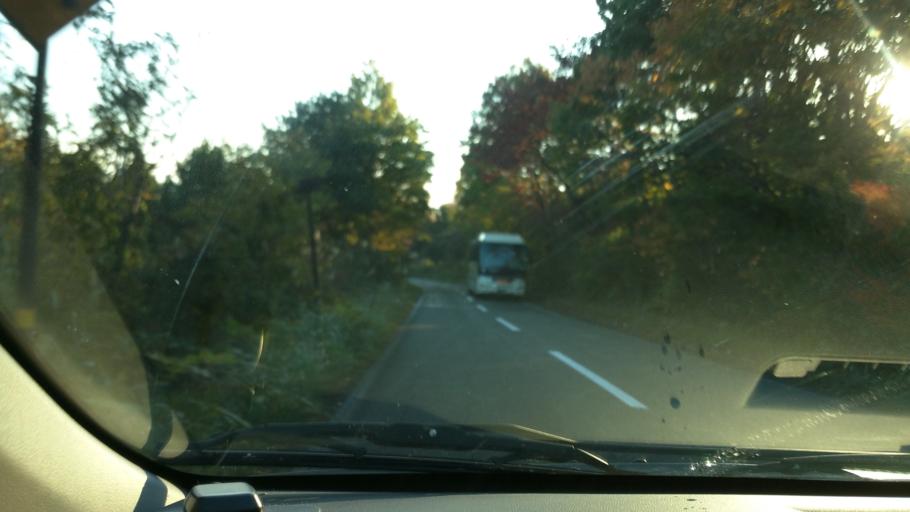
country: JP
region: Fukushima
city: Inawashiro
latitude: 37.5822
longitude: 140.0274
